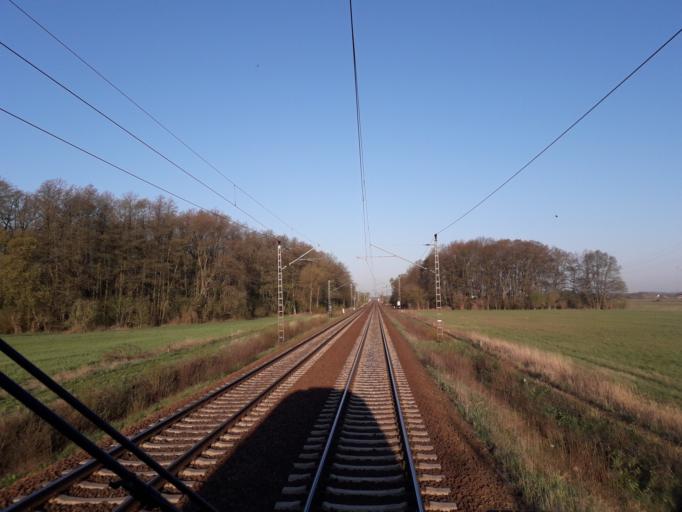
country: DE
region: Brandenburg
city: Stahnsdorf
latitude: 52.3200
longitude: 13.1851
